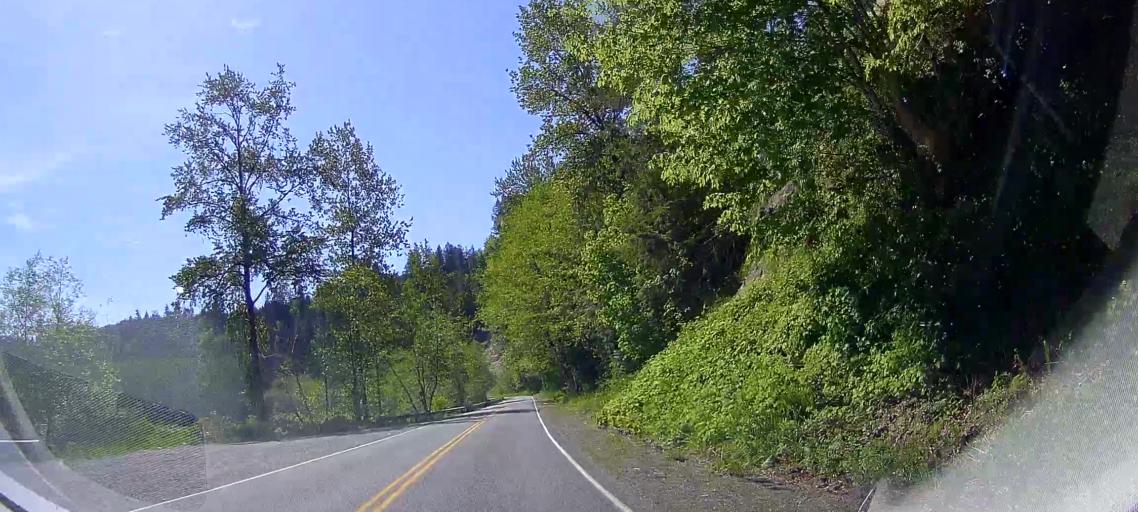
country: US
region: Washington
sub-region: Snohomish County
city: Darrington
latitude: 48.5086
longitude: -121.7225
